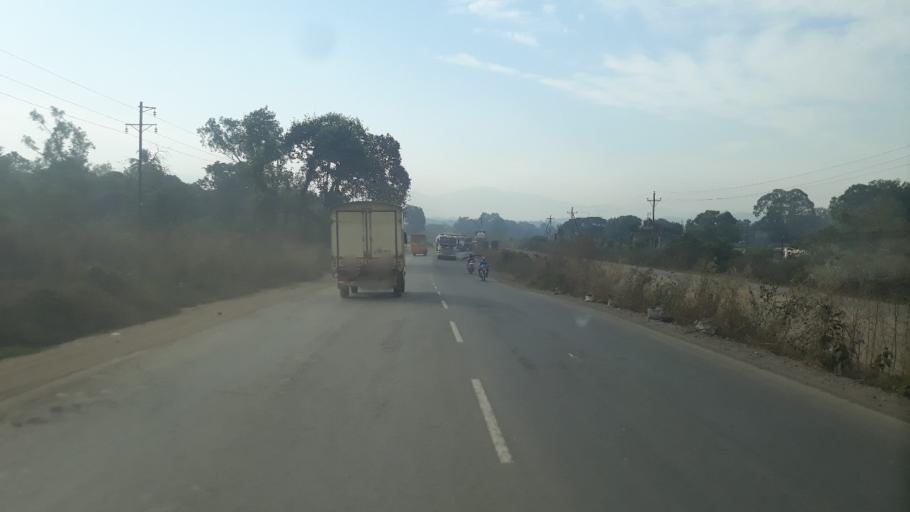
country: IN
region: Maharashtra
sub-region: Raigarh
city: Pen
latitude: 18.7694
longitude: 73.0916
